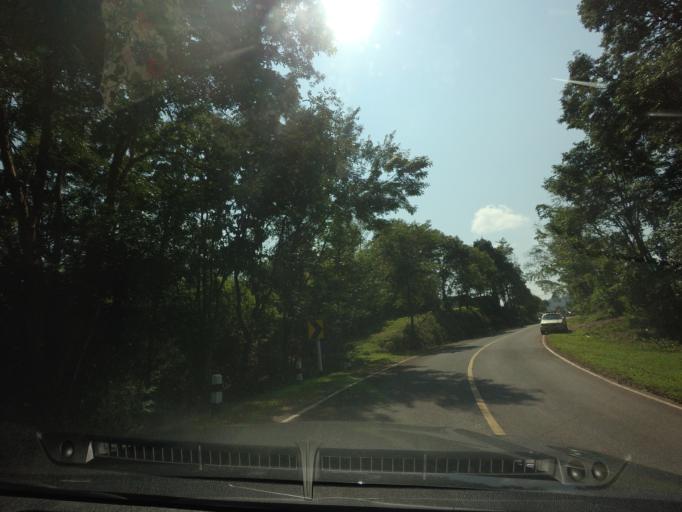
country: TH
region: Nan
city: Bo Kluea
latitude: 19.0643
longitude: 101.1672
